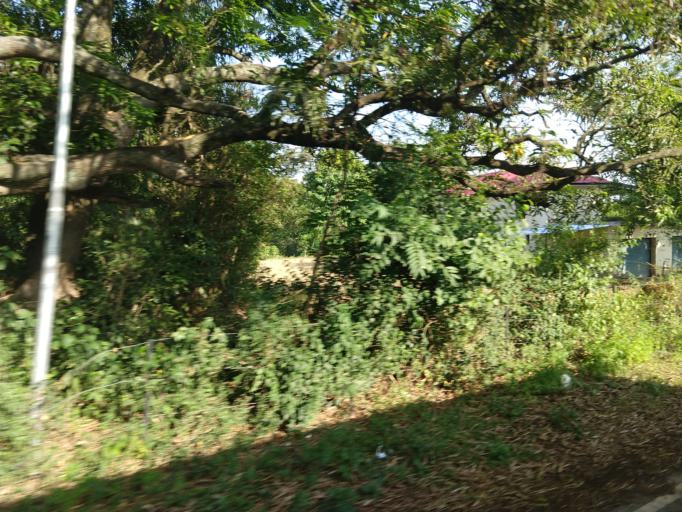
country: IN
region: Himachal Pradesh
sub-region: Chamba
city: Chowari
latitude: 32.3587
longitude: 75.9206
